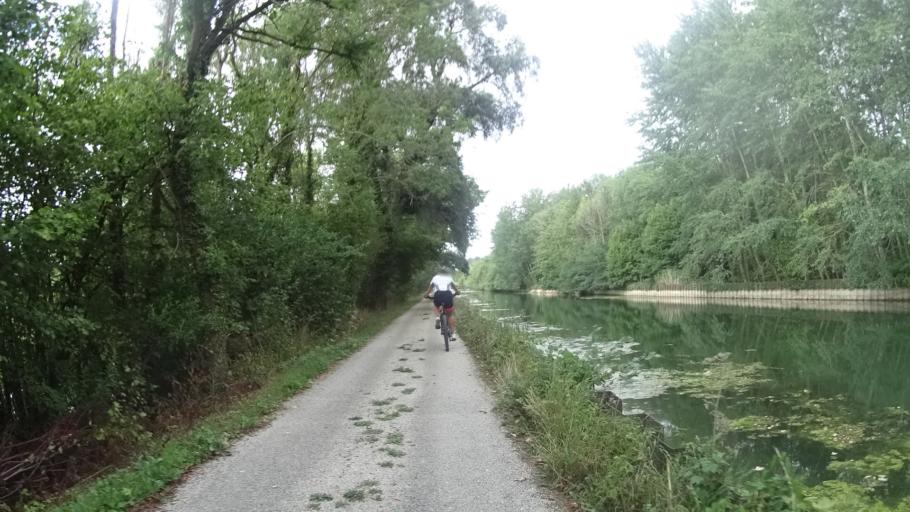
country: FR
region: Picardie
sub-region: Departement de l'Aisne
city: Itancourt
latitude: 49.7583
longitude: 3.3812
